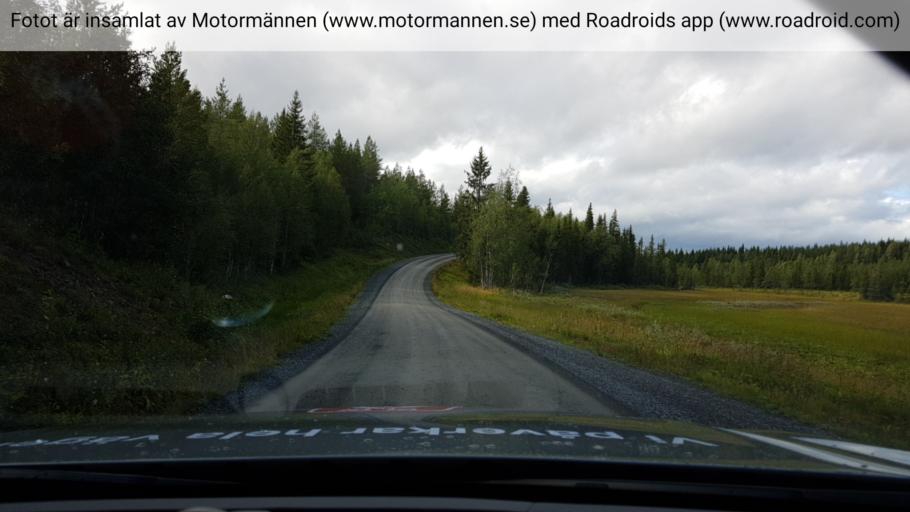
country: SE
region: Jaemtland
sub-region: Krokoms Kommun
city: Krokom
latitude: 63.7350
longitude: 14.4932
